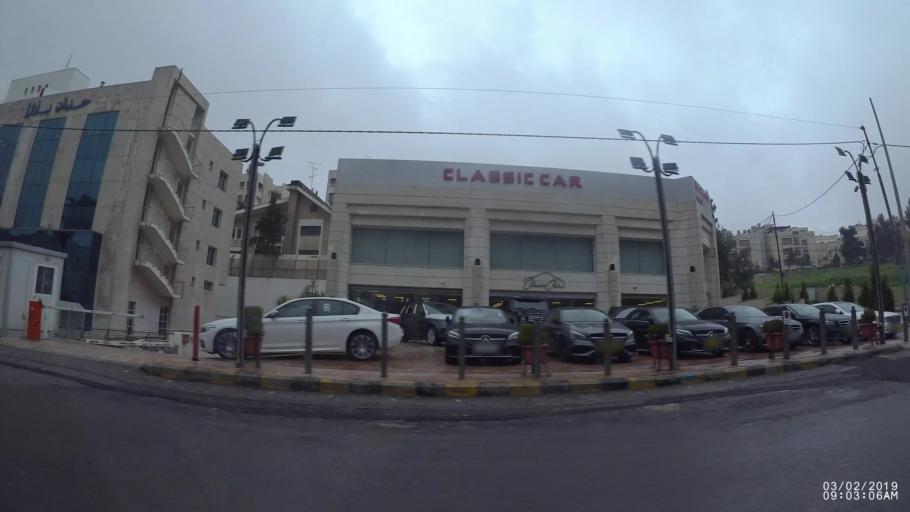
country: JO
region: Amman
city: Amman
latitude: 31.9604
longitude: 35.8932
